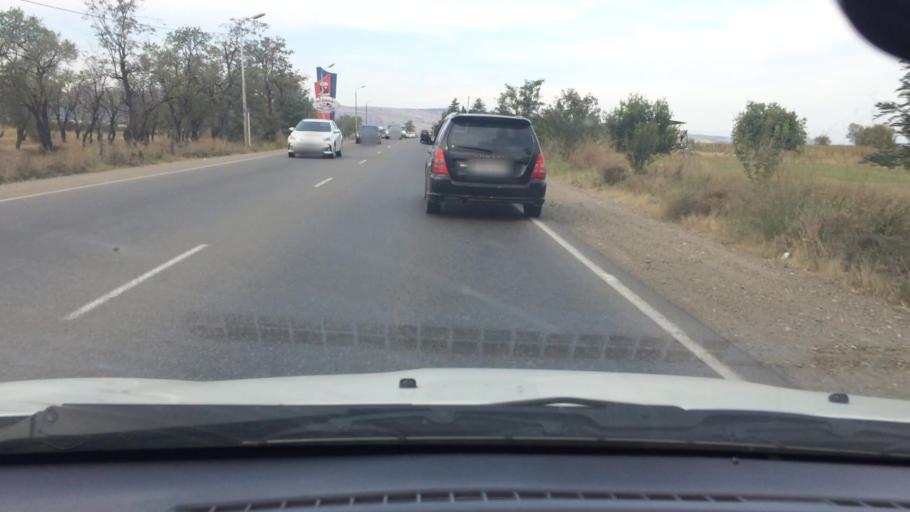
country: GE
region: Kvemo Kartli
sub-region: Marneuli
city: Marneuli
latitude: 41.5896
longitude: 44.7799
